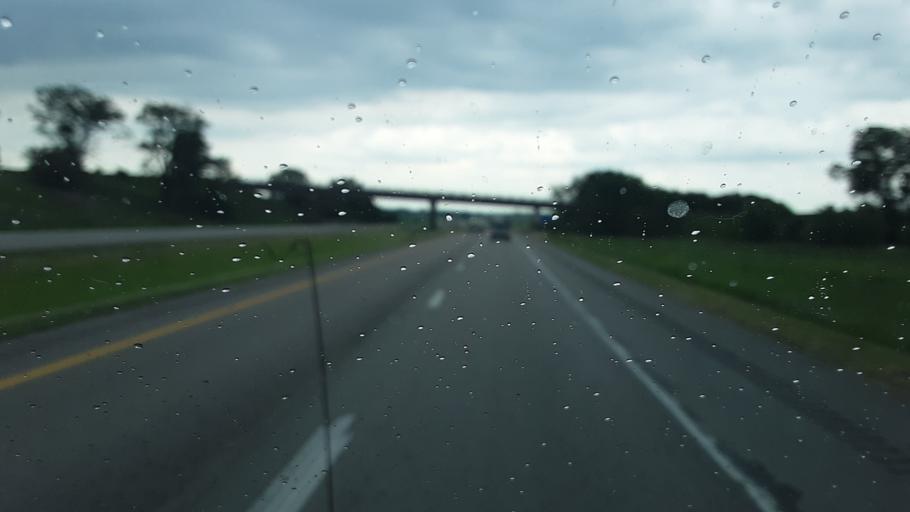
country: US
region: Iowa
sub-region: Pottawattamie County
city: Council Bluffs
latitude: 41.3491
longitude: -95.7032
